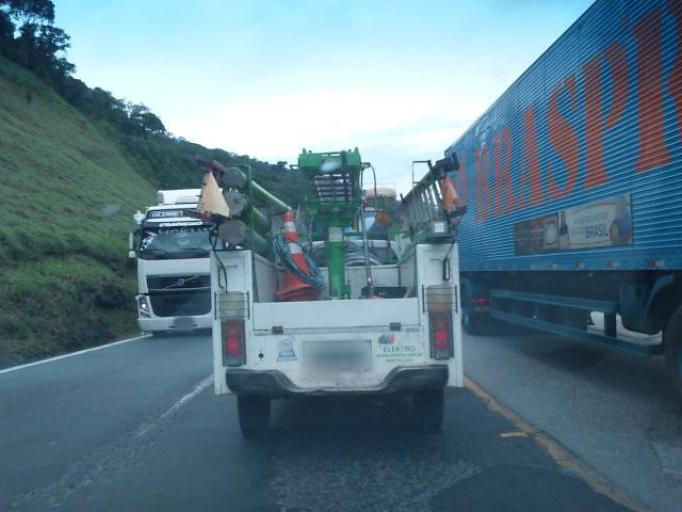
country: BR
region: Sao Paulo
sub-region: Juquitiba
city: Juquitiba
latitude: -24.0569
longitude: -47.2158
